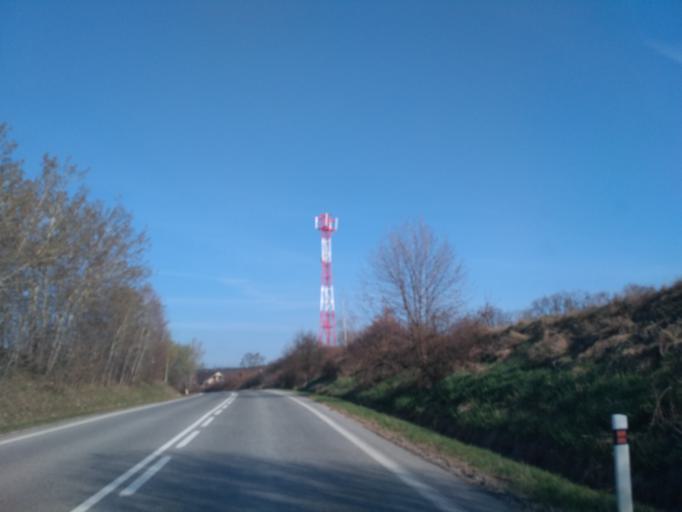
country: SK
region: Kosicky
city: Moldava nad Bodvou
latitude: 48.6741
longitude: 21.1092
